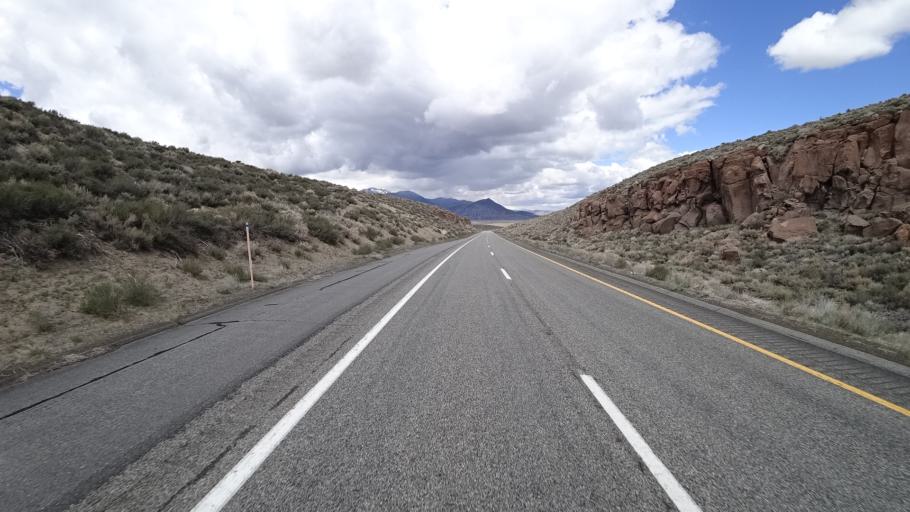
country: US
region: California
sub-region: Mono County
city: Mammoth Lakes
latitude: 37.8519
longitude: -119.0831
